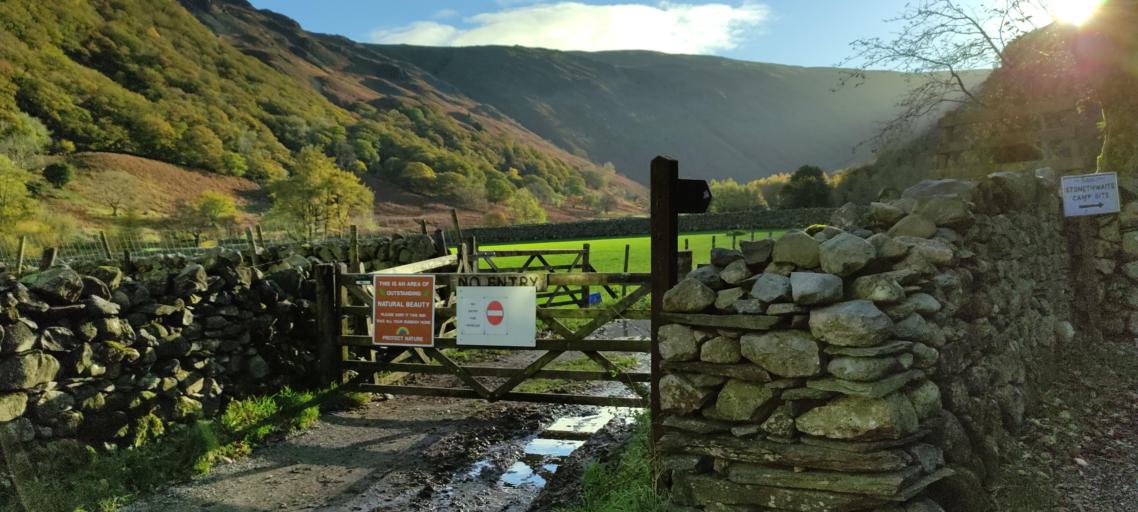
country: GB
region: England
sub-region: Cumbria
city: Keswick
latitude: 54.5128
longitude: -3.1399
